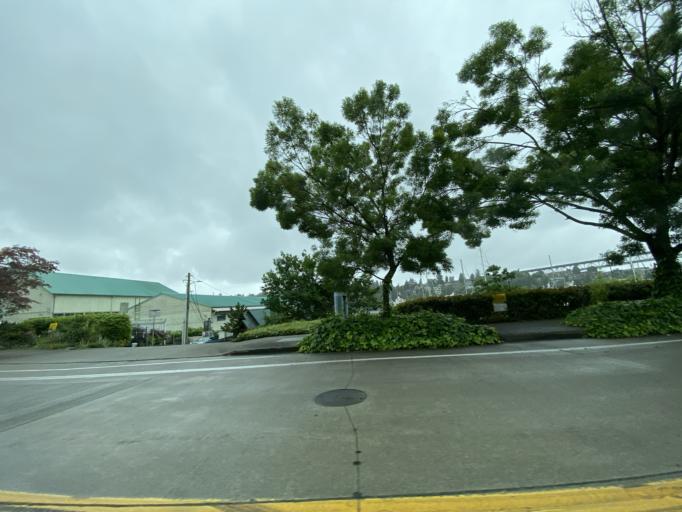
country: US
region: Washington
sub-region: King County
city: Seattle
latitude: 47.6510
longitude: -122.3132
